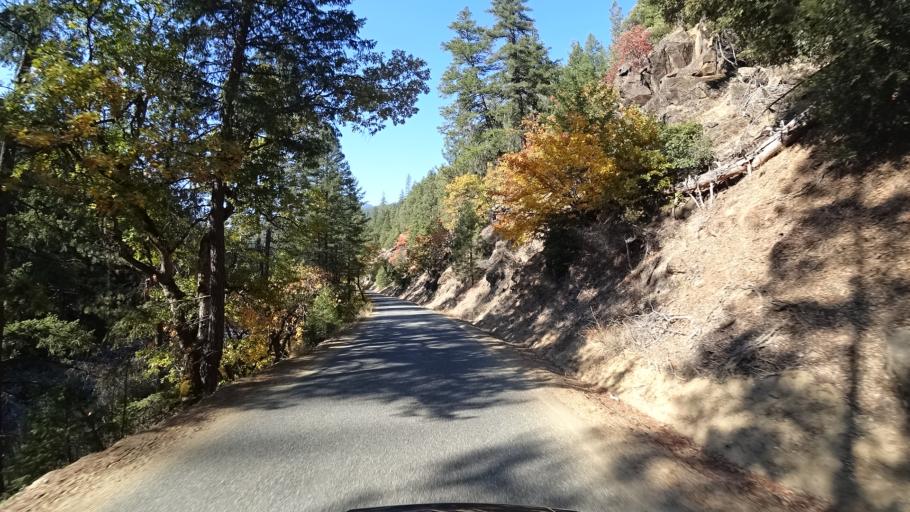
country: US
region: California
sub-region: Siskiyou County
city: Happy Camp
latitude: 41.6353
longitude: -123.0982
